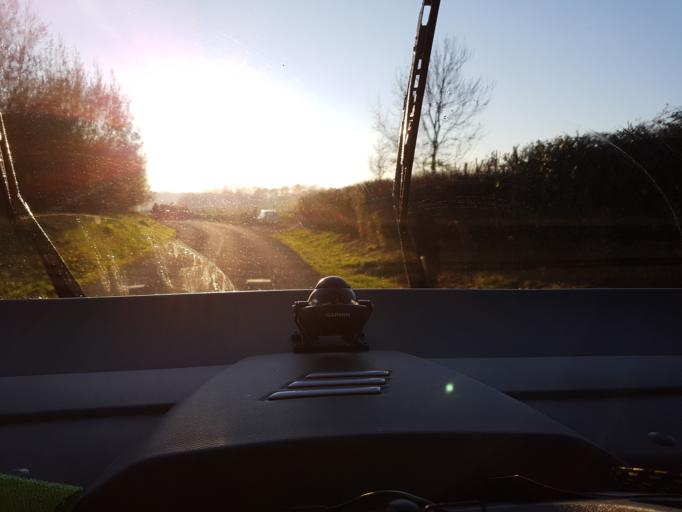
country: FR
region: Nord-Pas-de-Calais
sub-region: Departement du Pas-de-Calais
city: Wailly
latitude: 50.5228
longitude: 1.9590
